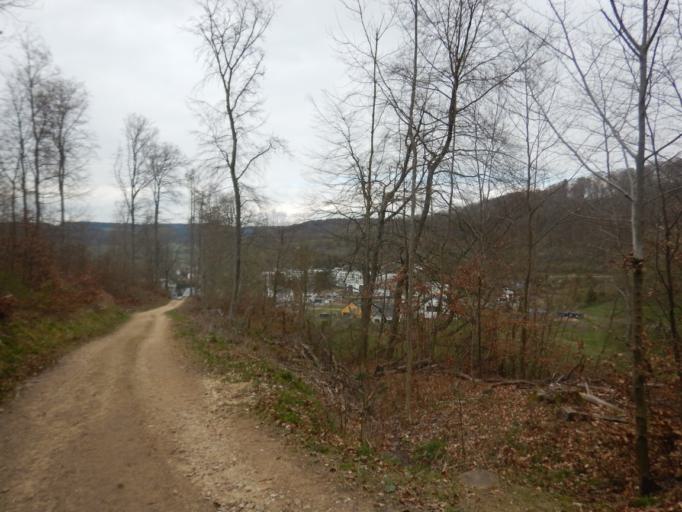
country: LU
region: Luxembourg
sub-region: Canton de Mersch
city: Lorentzweiler
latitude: 49.6998
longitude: 6.1540
